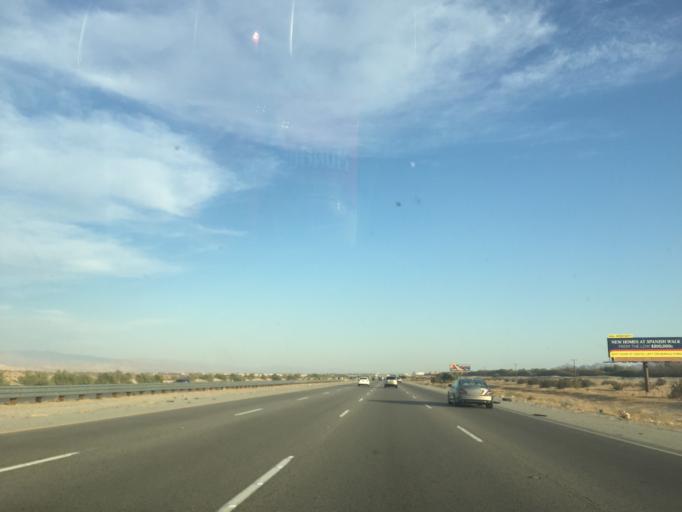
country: US
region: California
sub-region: Riverside County
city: Thousand Palms
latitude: 33.8389
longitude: -116.4412
